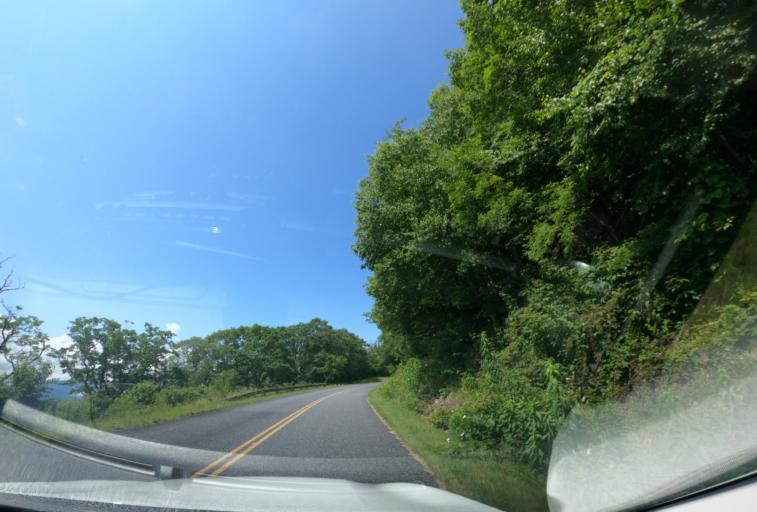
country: US
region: North Carolina
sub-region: Haywood County
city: Maggie Valley
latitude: 35.4516
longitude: -83.0988
